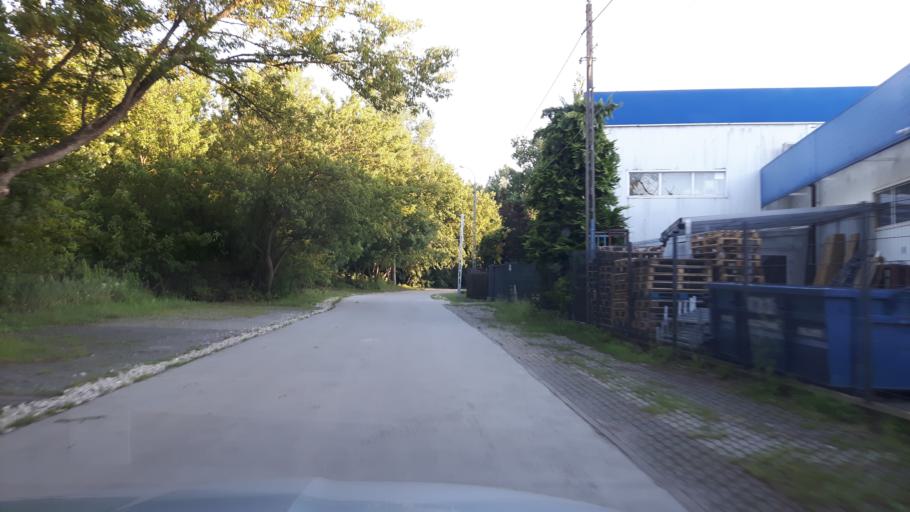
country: PL
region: Masovian Voivodeship
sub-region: Warszawa
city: Praga Poludnie
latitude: 52.2703
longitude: 21.0854
